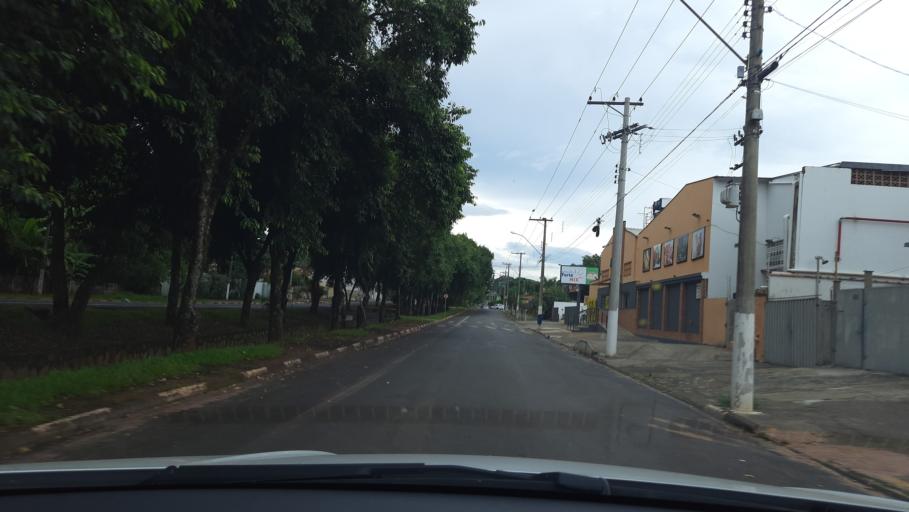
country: BR
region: Sao Paulo
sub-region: Casa Branca
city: Casa Branca
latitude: -21.7693
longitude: -47.0862
